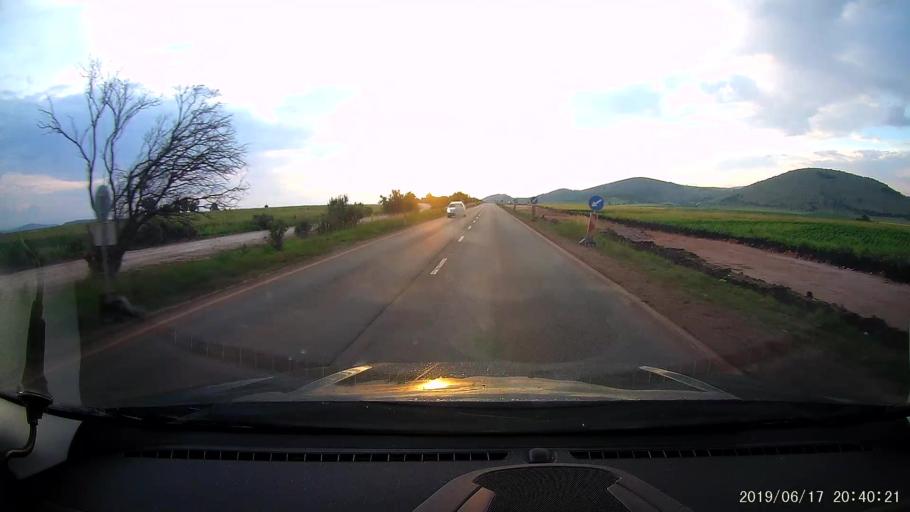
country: BG
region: Sofiya
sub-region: Obshtina Slivnitsa
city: Slivnitsa
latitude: 42.8859
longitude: 22.9882
